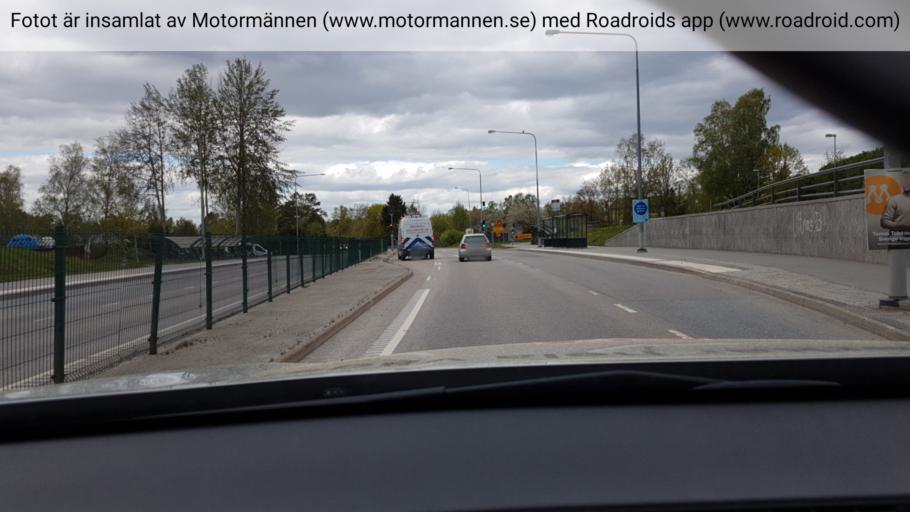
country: SE
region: Stockholm
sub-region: Tyreso Kommun
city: Bollmora
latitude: 59.2132
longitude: 18.2086
